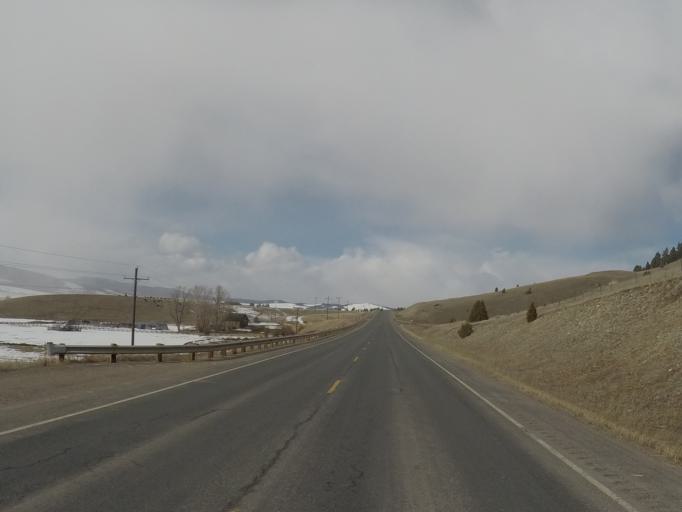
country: US
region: Montana
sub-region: Granite County
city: Philipsburg
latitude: 46.2854
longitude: -113.3226
